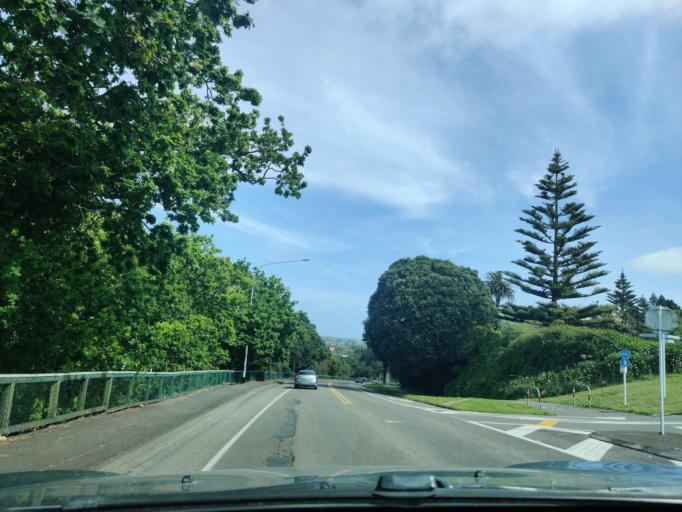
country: NZ
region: Manawatu-Wanganui
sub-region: Wanganui District
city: Wanganui
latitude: -39.9200
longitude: 175.0390
